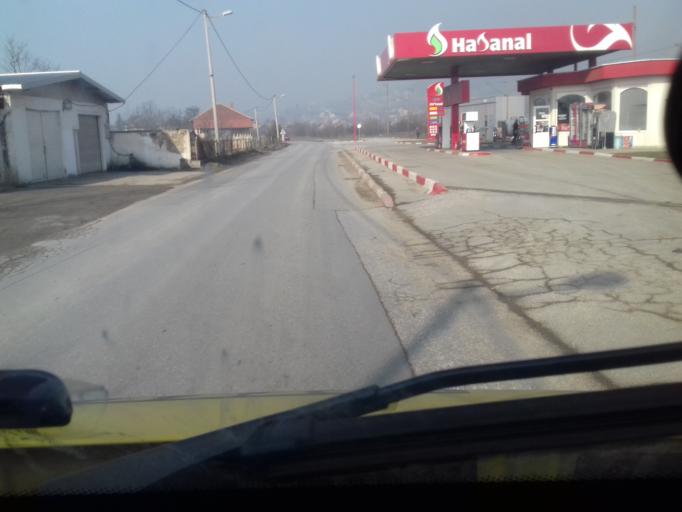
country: BA
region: Federation of Bosnia and Herzegovina
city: Ilijas
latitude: 43.9628
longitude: 18.2637
